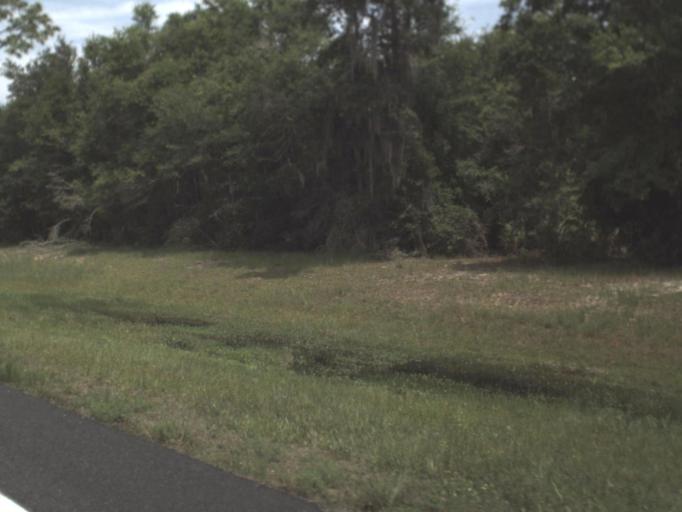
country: US
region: Florida
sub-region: Alachua County
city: Gainesville
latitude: 29.6047
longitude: -82.2151
